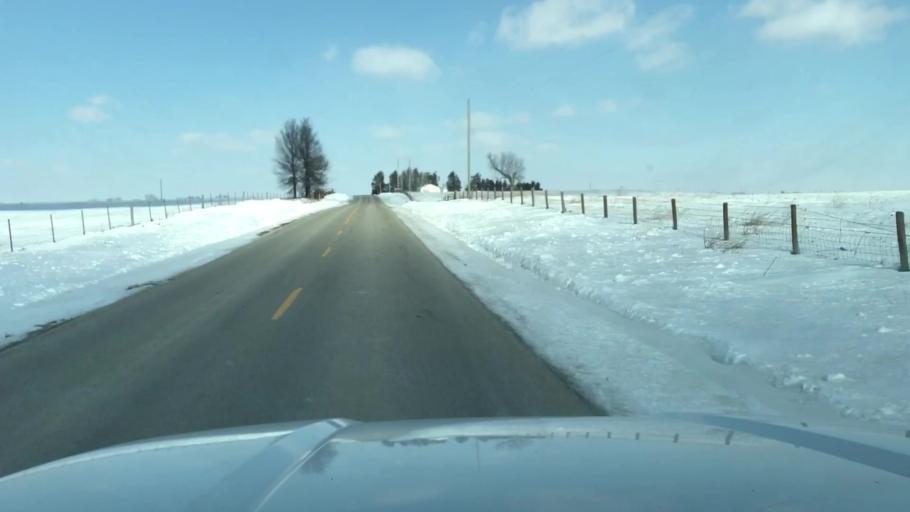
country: US
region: Missouri
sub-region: Nodaway County
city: Maryville
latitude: 40.3701
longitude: -94.7216
